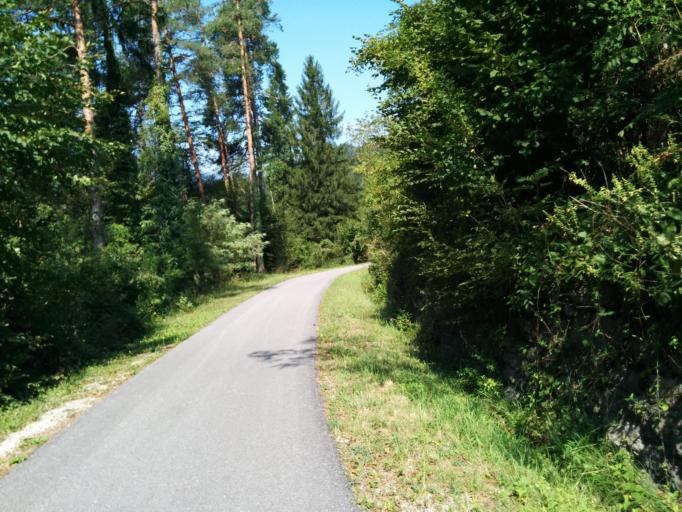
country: IT
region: Friuli Venezia Giulia
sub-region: Provincia di Udine
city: Raveo
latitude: 46.4299
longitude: 12.8970
